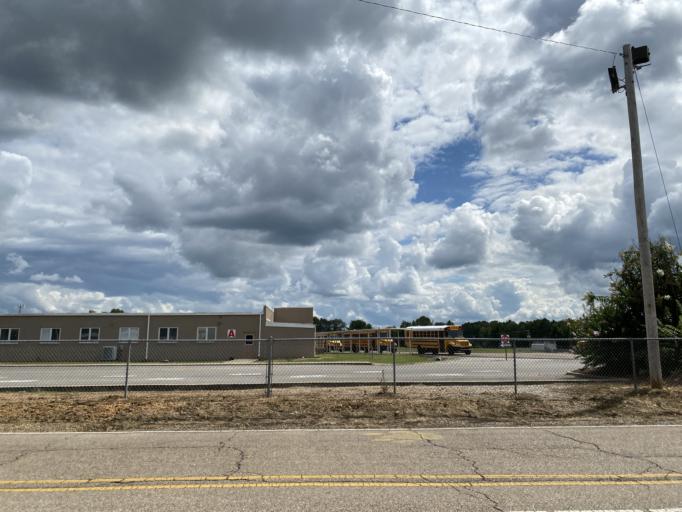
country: US
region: Mississippi
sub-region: Monroe County
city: Amory
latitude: 33.9769
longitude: -88.4173
